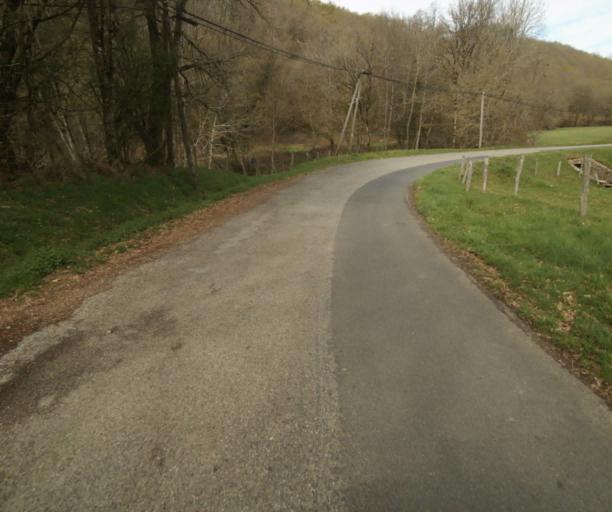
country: FR
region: Limousin
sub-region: Departement de la Correze
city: Laguenne
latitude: 45.2357
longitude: 1.8459
